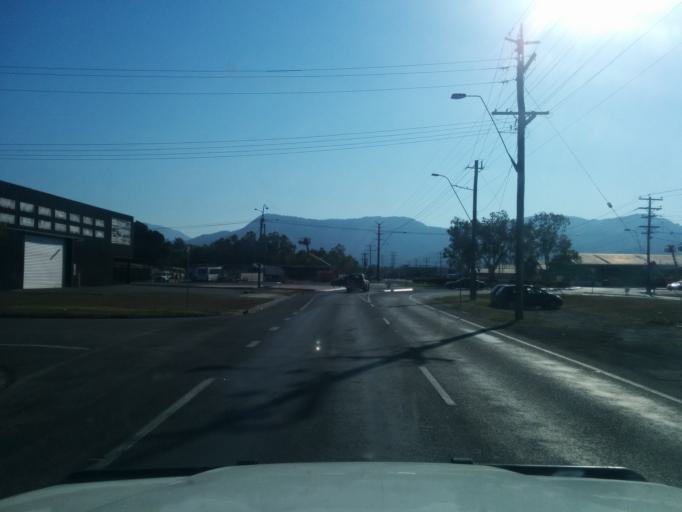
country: AU
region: Queensland
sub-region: Cairns
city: Woree
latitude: -16.9418
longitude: 145.7589
